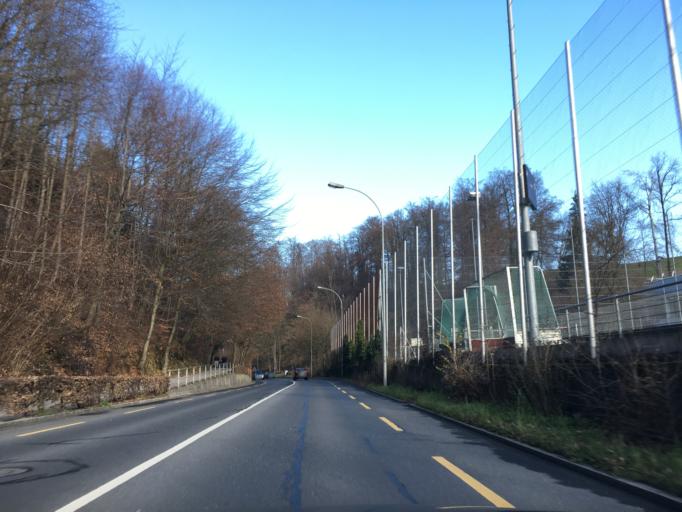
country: CH
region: Lucerne
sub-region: Lucerne-Stadt District
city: Luzern
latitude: 47.0614
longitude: 8.3244
